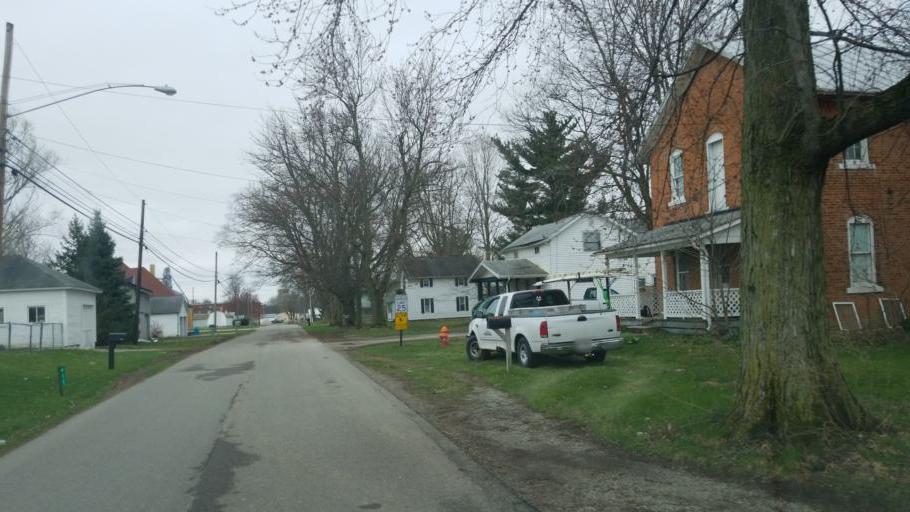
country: US
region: Ohio
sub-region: Wyandot County
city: Upper Sandusky
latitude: 40.8220
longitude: -83.1315
